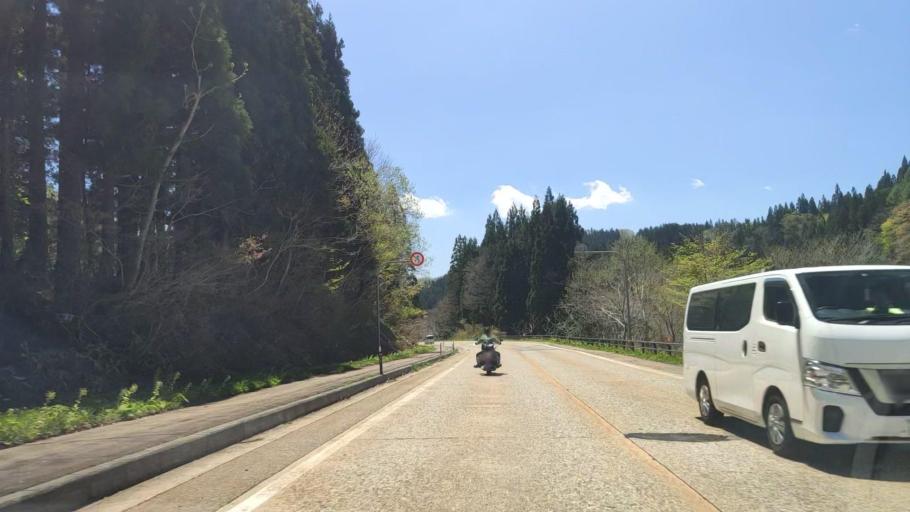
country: JP
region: Akita
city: Yuzawa
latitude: 38.9966
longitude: 140.3637
